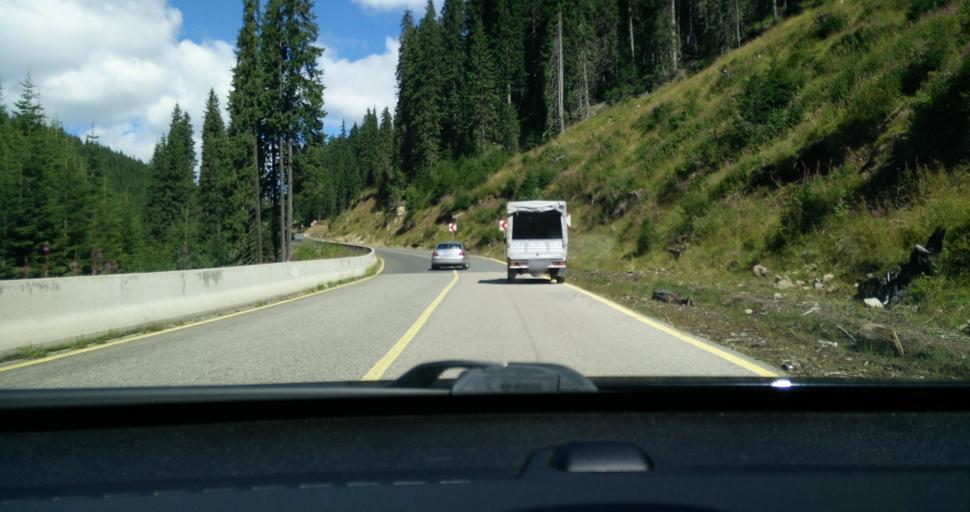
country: RO
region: Hunedoara
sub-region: Oras Petrila
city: Petrila
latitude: 45.4401
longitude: 23.6278
